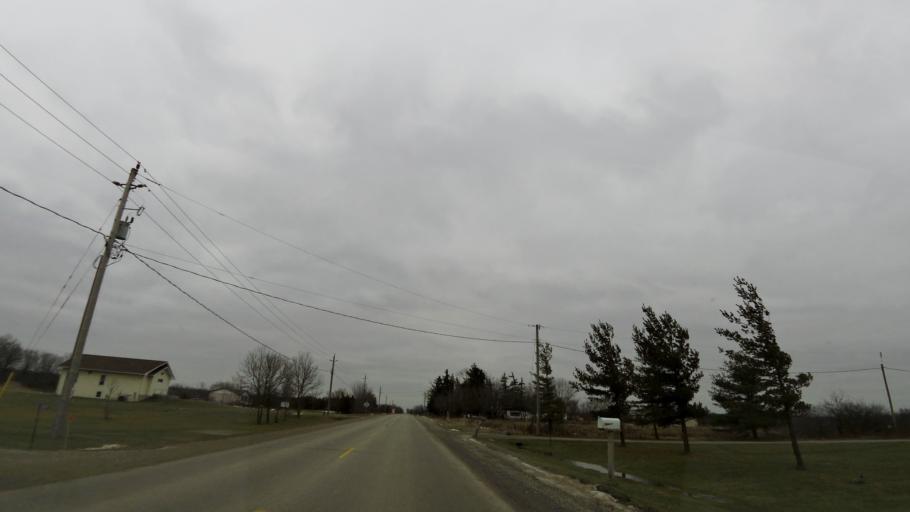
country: CA
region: Ontario
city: Ancaster
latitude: 43.0583
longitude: -80.0896
